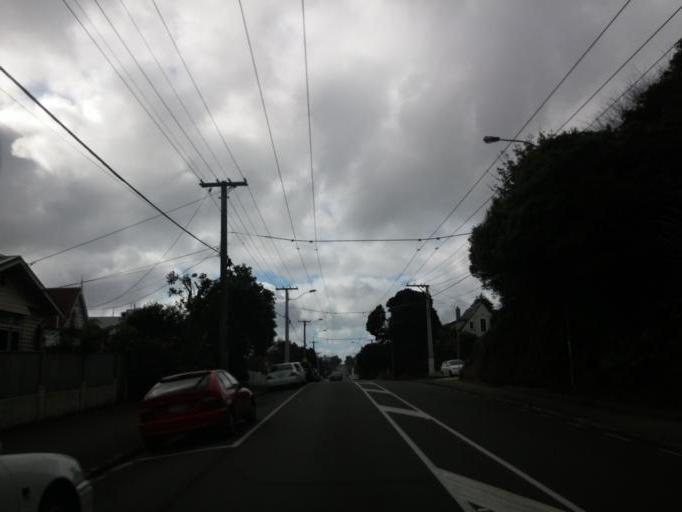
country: NZ
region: Wellington
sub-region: Wellington City
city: Kelburn
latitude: -41.2860
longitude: 174.7327
